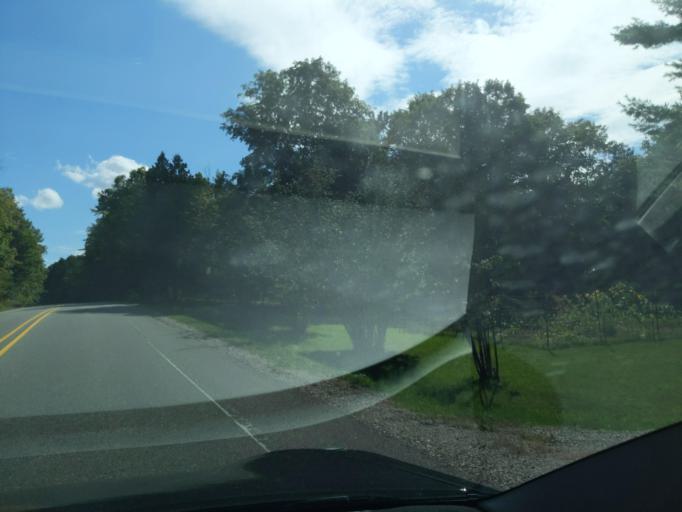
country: US
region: Michigan
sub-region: Antrim County
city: Bellaire
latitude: 45.0562
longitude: -85.3189
